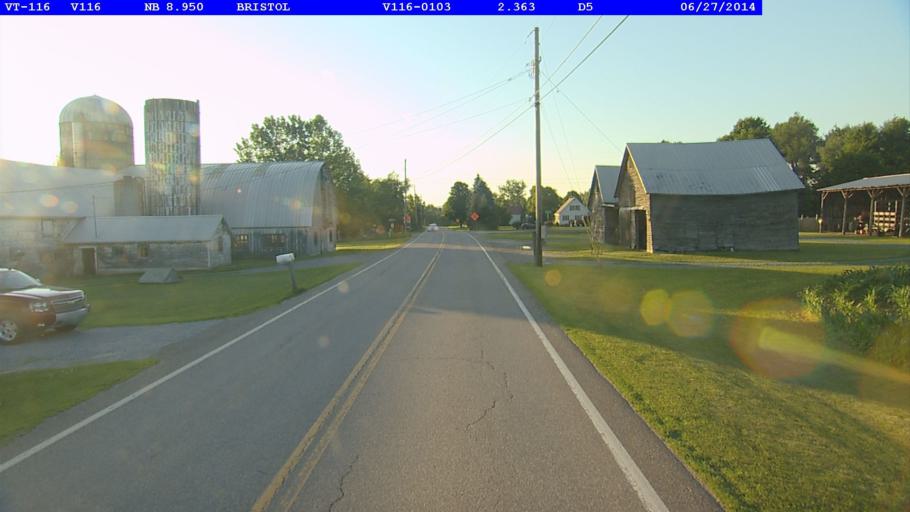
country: US
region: Vermont
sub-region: Addison County
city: Bristol
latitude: 44.0873
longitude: -73.0901
